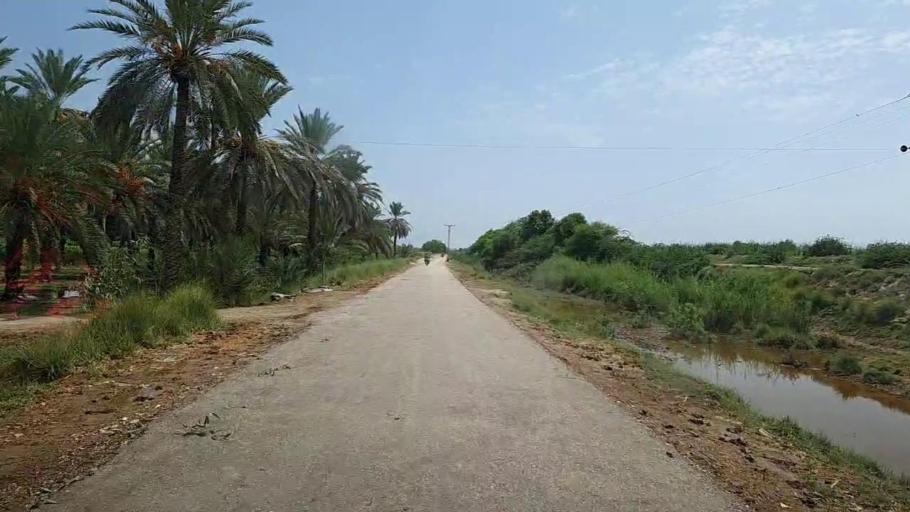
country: PK
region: Sindh
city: Bhiria
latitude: 26.9014
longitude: 68.1991
